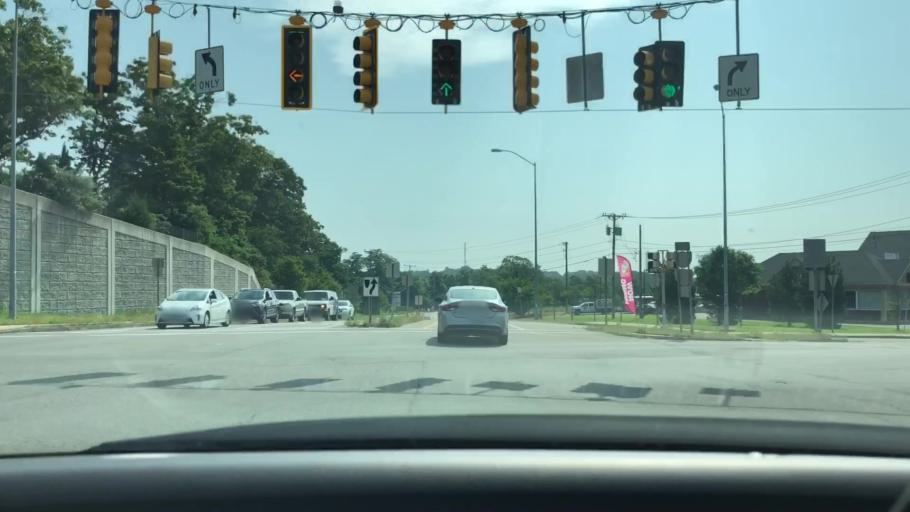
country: US
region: Massachusetts
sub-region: Barnstable County
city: Sagamore
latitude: 41.7823
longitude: -70.5411
